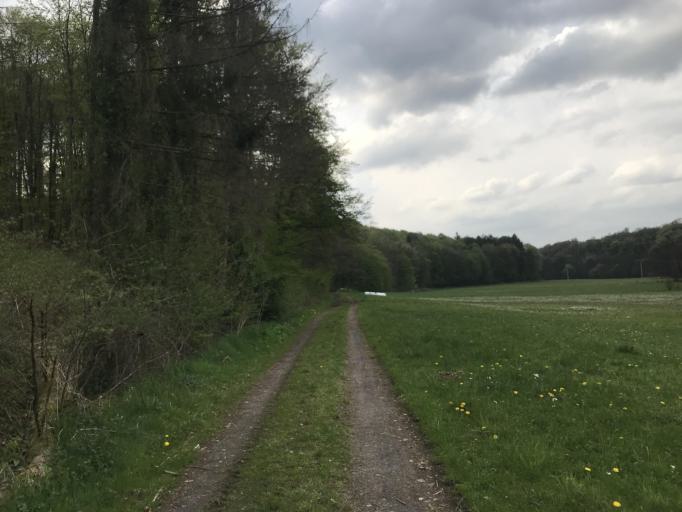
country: DE
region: Hesse
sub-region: Regierungsbezirk Giessen
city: Laubach
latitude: 50.5160
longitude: 8.9970
